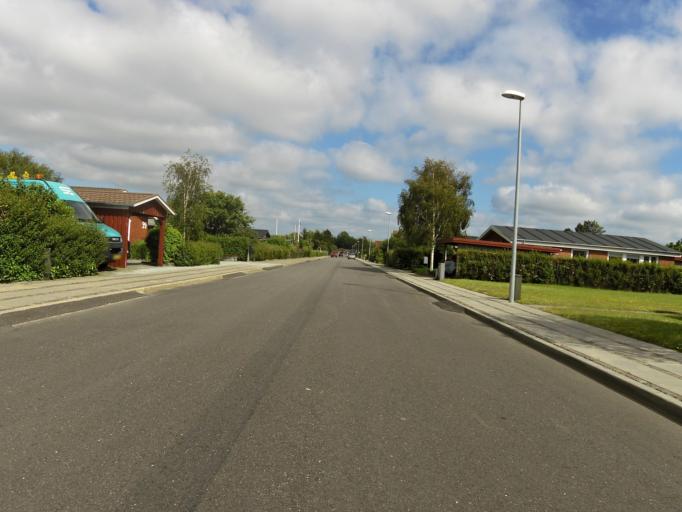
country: DK
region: South Denmark
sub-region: Esbjerg Kommune
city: Ribe
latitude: 55.3290
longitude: 8.7894
